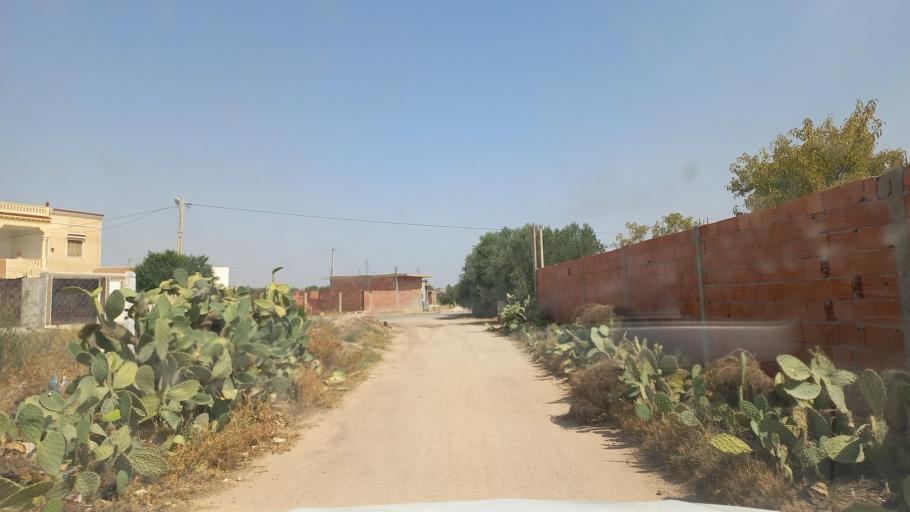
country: TN
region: Al Qasrayn
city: Kasserine
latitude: 35.2485
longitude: 9.0215
